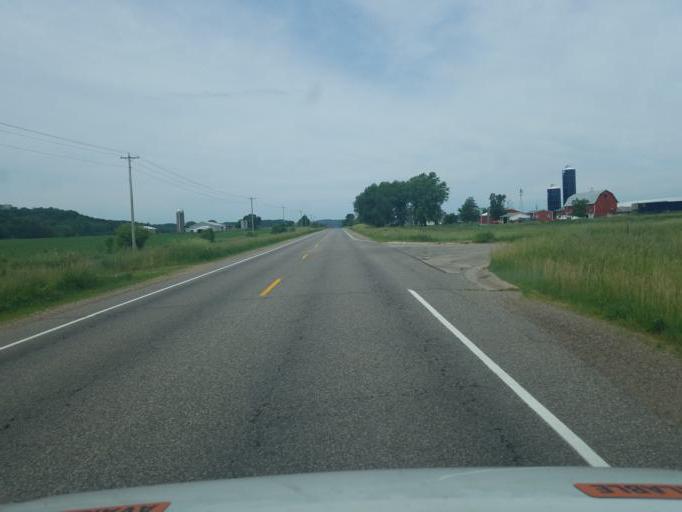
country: US
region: Wisconsin
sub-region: Juneau County
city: Mauston
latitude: 43.7891
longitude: -90.1212
